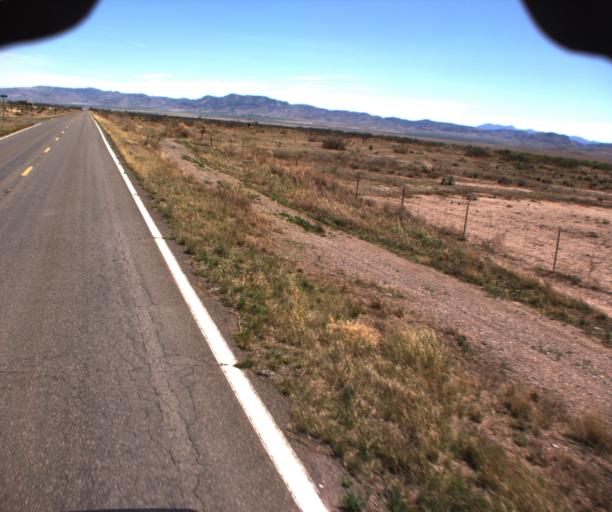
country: US
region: Arizona
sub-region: Cochise County
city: Douglas
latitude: 31.6321
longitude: -109.1959
